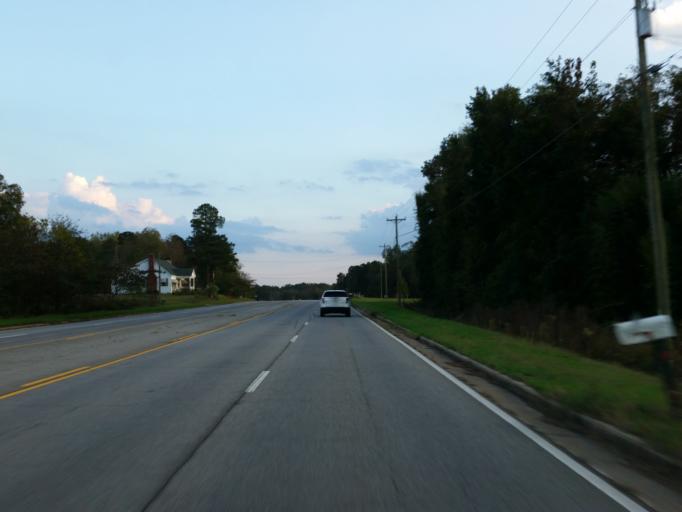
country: US
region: Georgia
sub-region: Houston County
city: Perry
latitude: 32.3757
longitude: -83.6185
